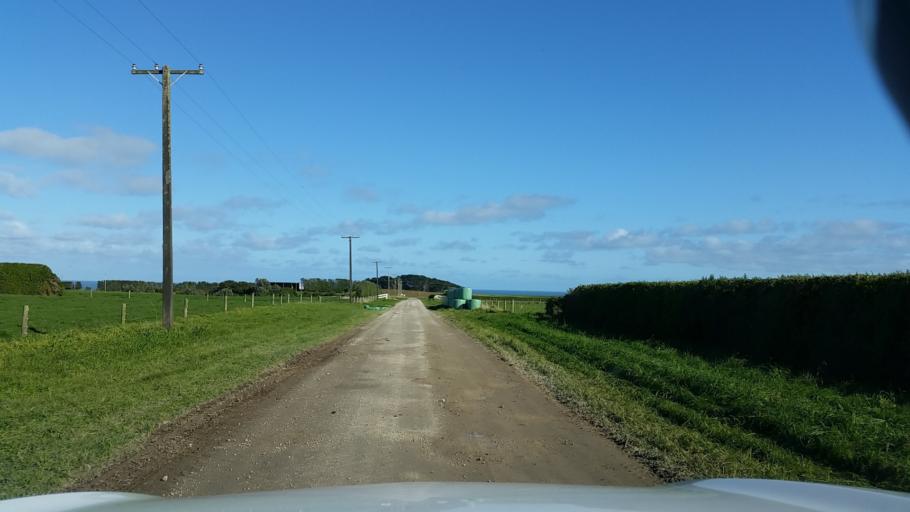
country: NZ
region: Taranaki
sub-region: South Taranaki District
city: Patea
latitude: -39.6844
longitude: 174.4000
